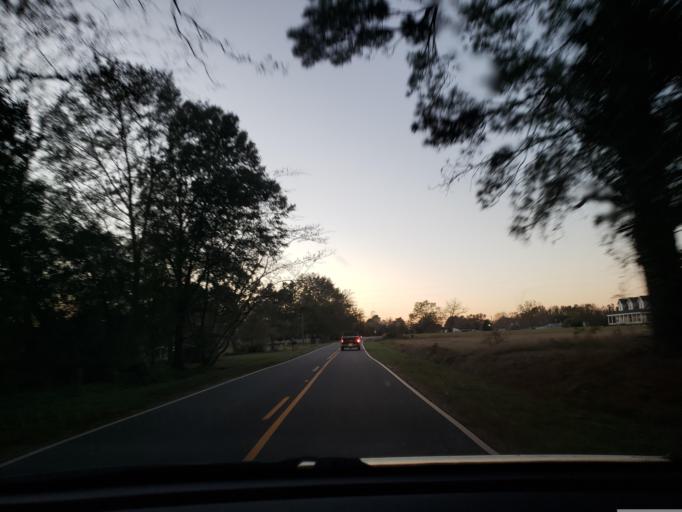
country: US
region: North Carolina
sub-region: Duplin County
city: Beulaville
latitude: 34.7969
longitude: -77.7744
